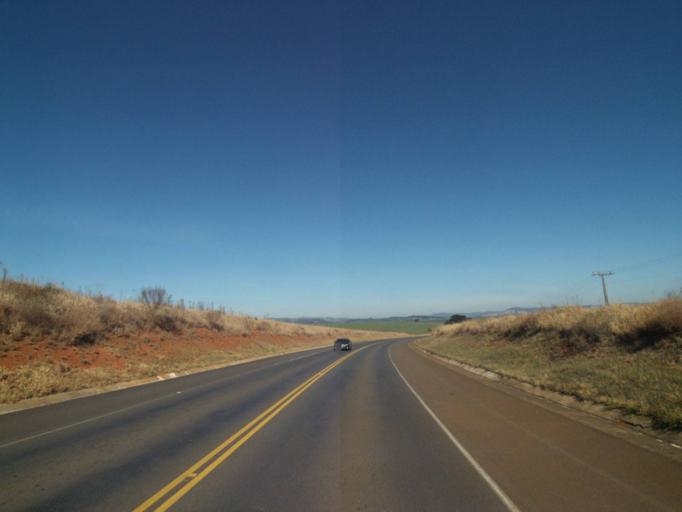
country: BR
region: Parana
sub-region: Tibagi
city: Tibagi
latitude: -24.4589
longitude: -50.4252
